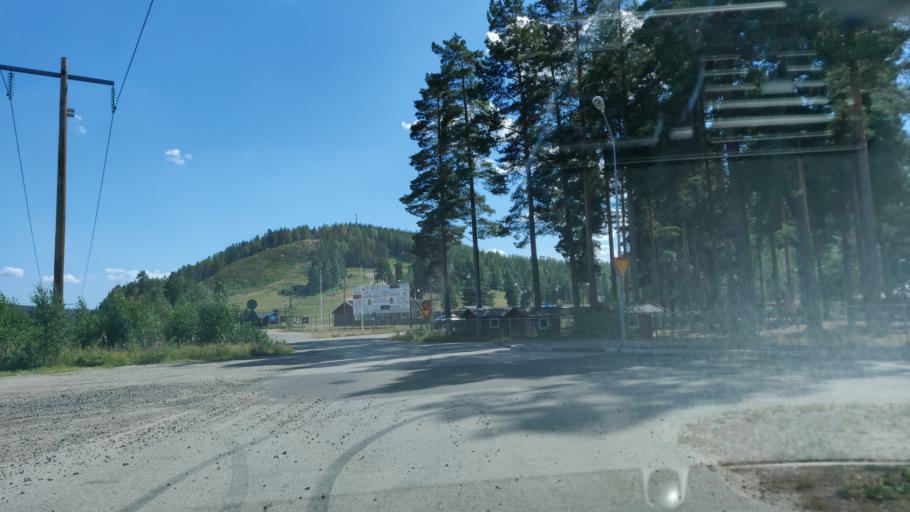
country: SE
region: Vaermland
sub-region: Hagfors Kommun
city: Ekshaerad
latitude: 60.1728
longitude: 13.4861
